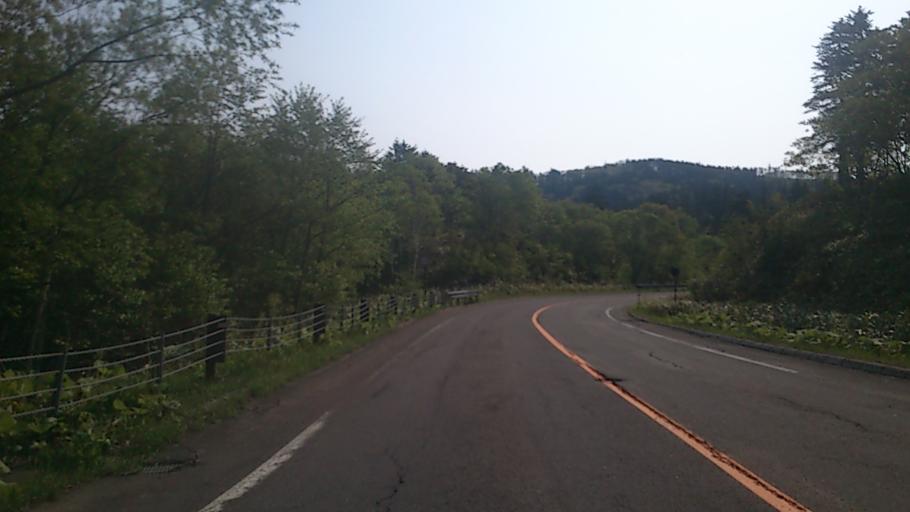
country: JP
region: Hokkaido
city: Bihoro
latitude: 43.4490
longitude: 144.2204
